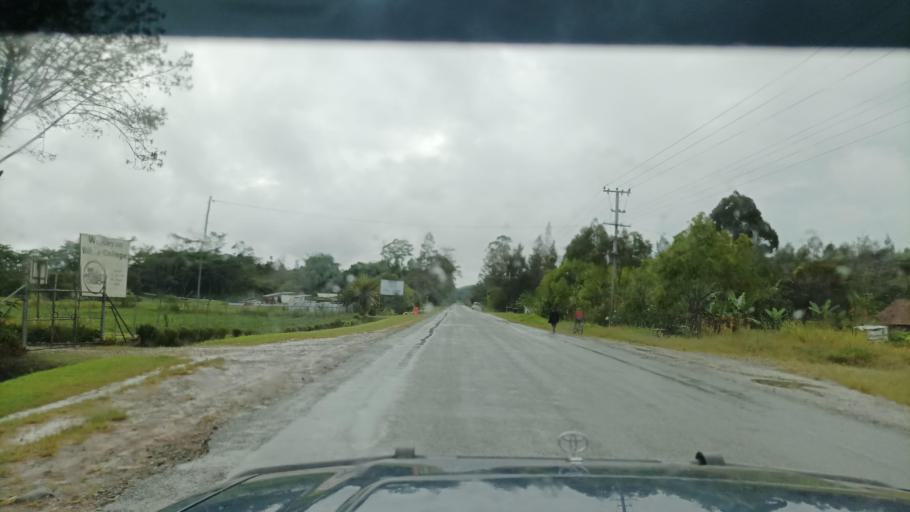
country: PG
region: Western Highlands
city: Rauna
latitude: -5.8232
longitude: 144.3969
